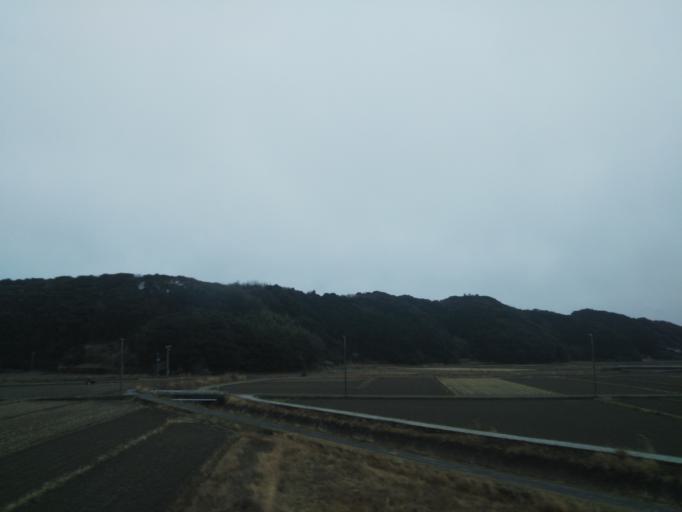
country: JP
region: Kochi
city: Nakamura
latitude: 32.9844
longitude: 132.9608
